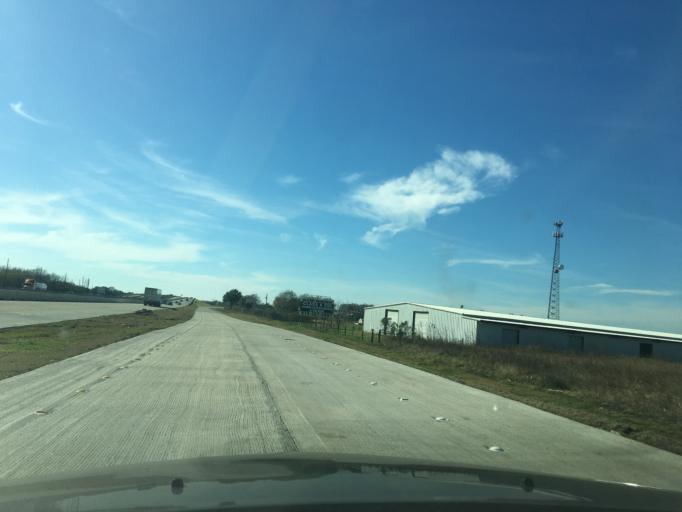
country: US
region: Texas
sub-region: Fort Bend County
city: Pleak
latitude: 29.4874
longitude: -95.9298
